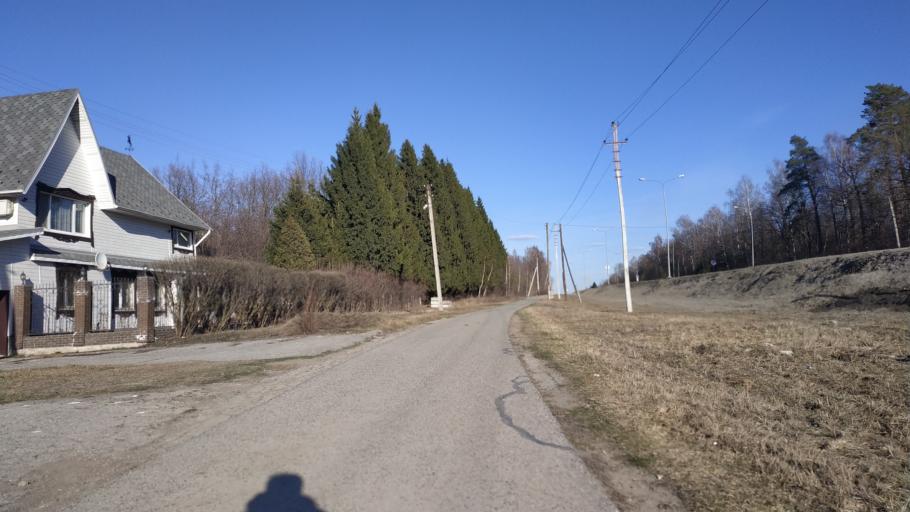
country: RU
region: Chuvashia
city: Novyye Lapsary
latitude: 56.1317
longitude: 47.1436
